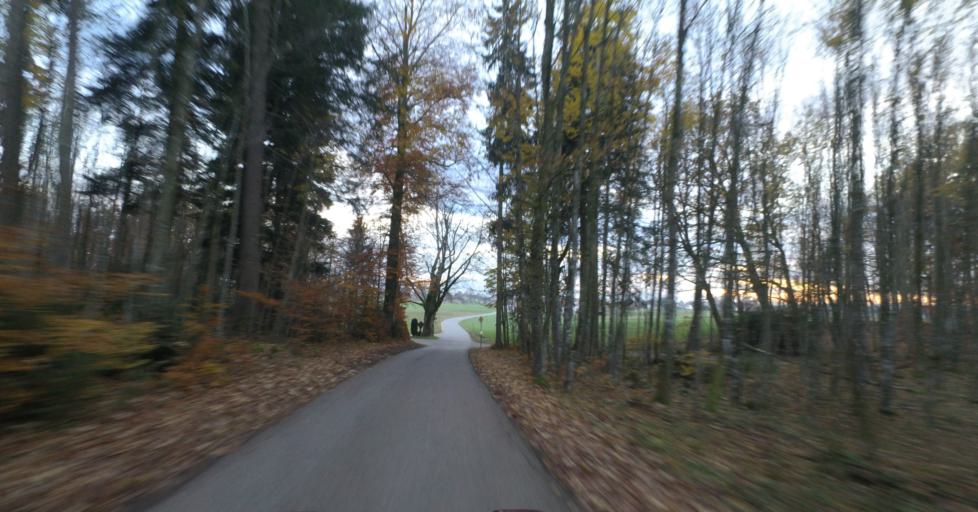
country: DE
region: Bavaria
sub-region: Upper Bavaria
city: Gstadt am Chiemsee
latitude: 47.8956
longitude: 12.4088
